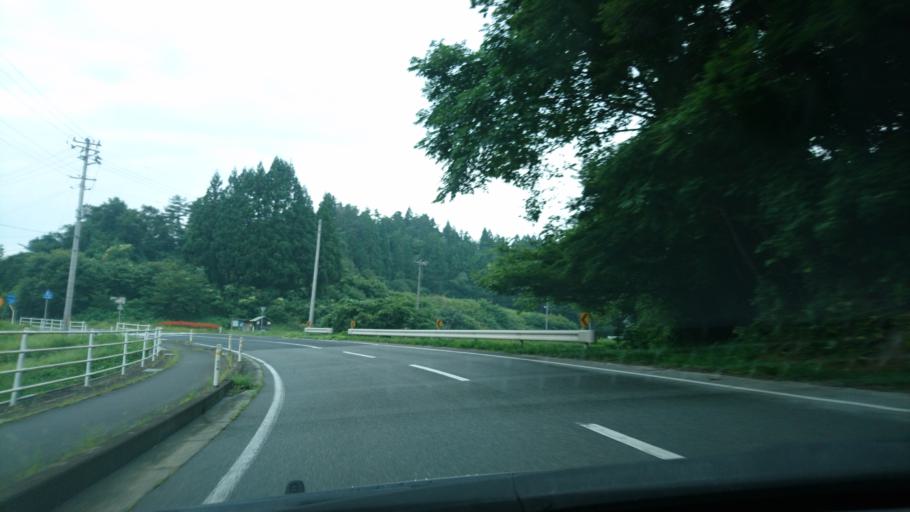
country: JP
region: Iwate
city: Ichinoseki
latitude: 39.0154
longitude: 141.2566
